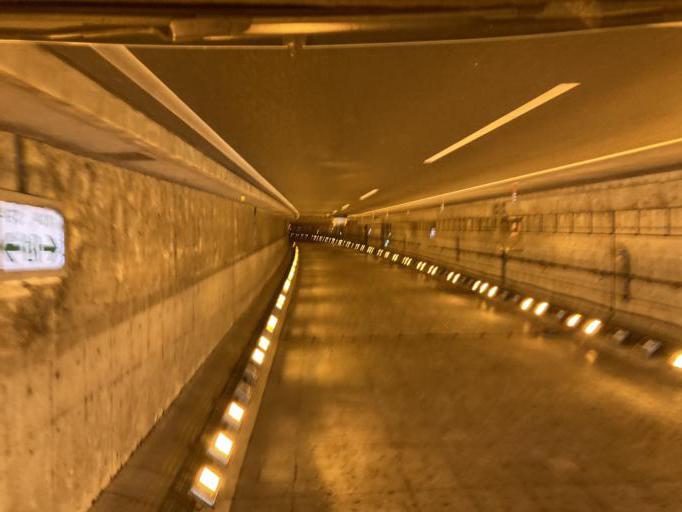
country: JP
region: Okinawa
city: Naha-shi
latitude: 26.2183
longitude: 127.6635
